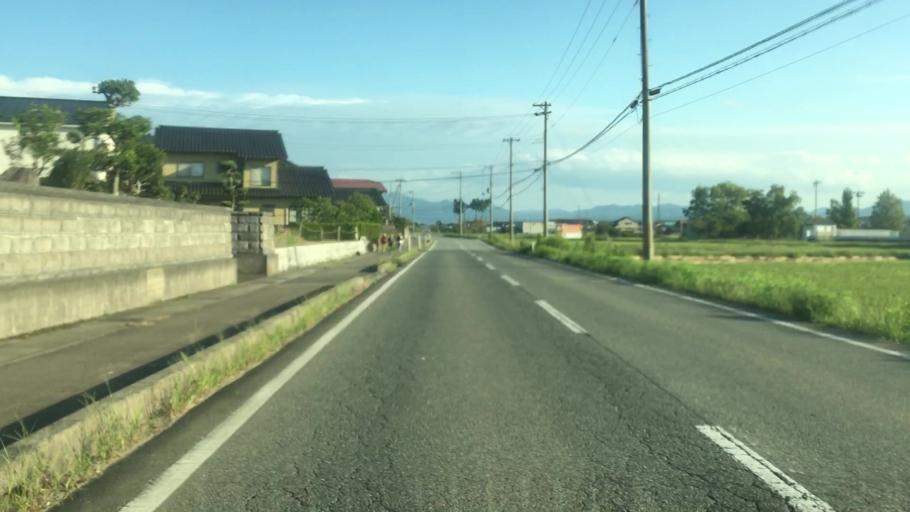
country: JP
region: Hyogo
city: Toyooka
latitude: 35.5644
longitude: 134.8203
